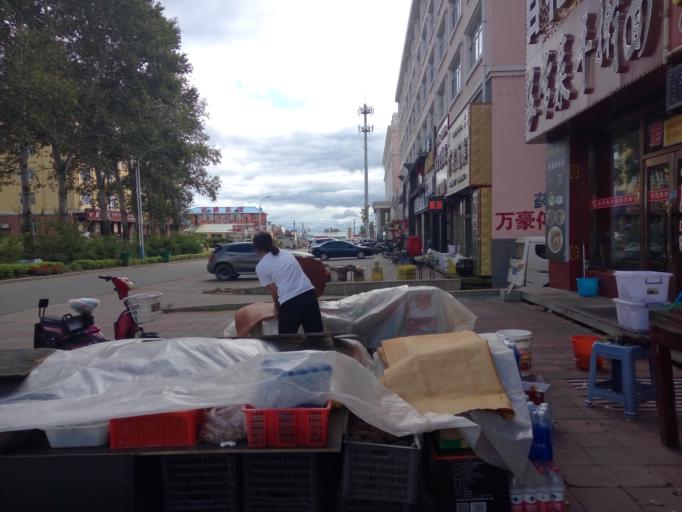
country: CN
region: Heilongjiang Sheng
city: Erjing
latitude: 48.6505
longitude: 126.1627
